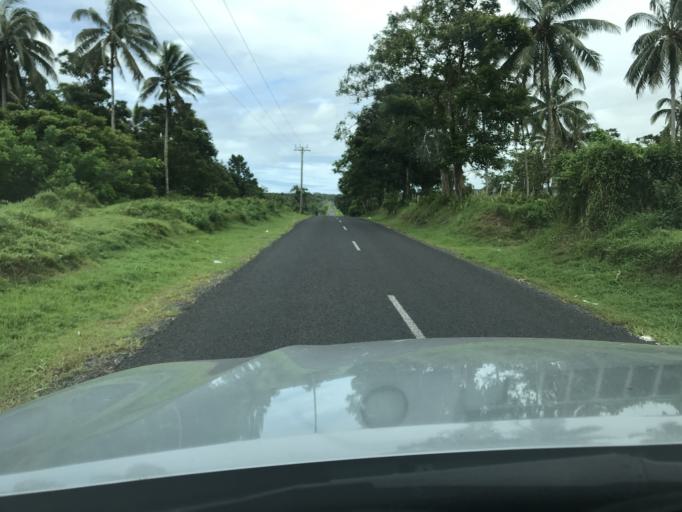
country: WS
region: A'ana
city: Satapuala
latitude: -13.8781
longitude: -171.9395
